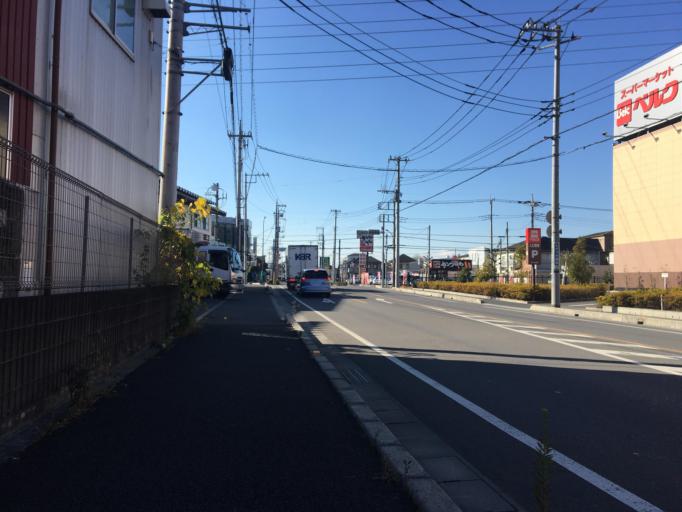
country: JP
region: Saitama
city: Yashio-shi
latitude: 35.8324
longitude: 139.8325
